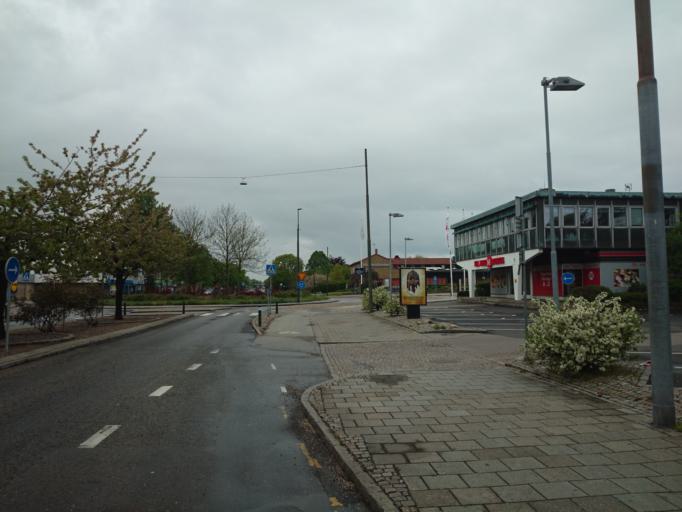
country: SE
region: Skane
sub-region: Malmo
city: Malmoe
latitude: 55.5946
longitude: 12.9667
